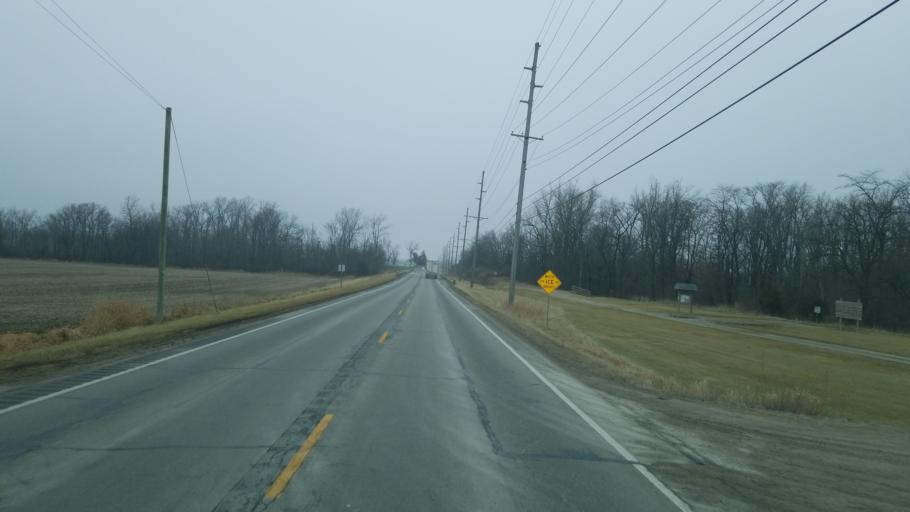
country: US
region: Indiana
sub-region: Adams County
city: Geneva
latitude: 40.5644
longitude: -84.9598
